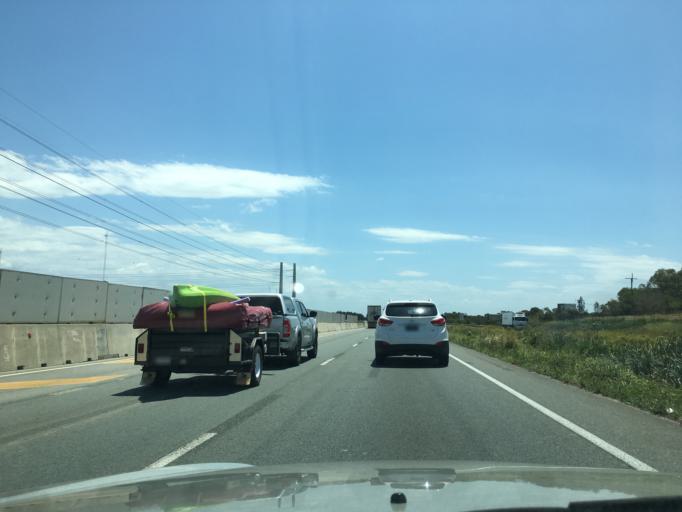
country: AU
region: Queensland
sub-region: Brisbane
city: Shorncliffe
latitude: -27.3601
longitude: 153.0935
